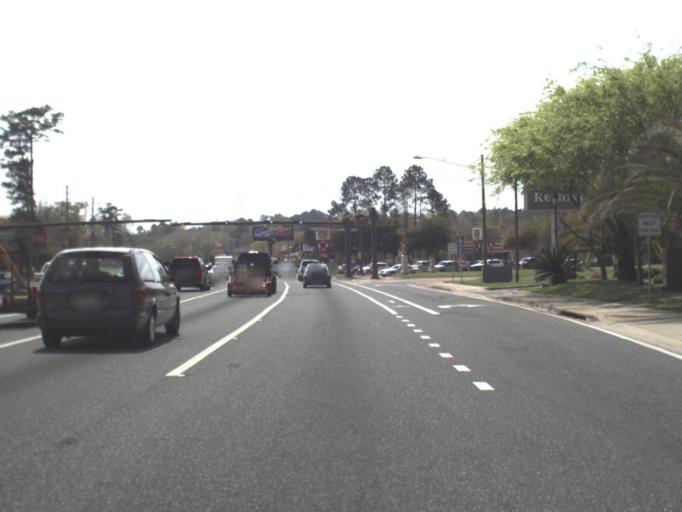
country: US
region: Florida
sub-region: Leon County
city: Tallahassee
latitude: 30.4793
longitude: -84.2369
